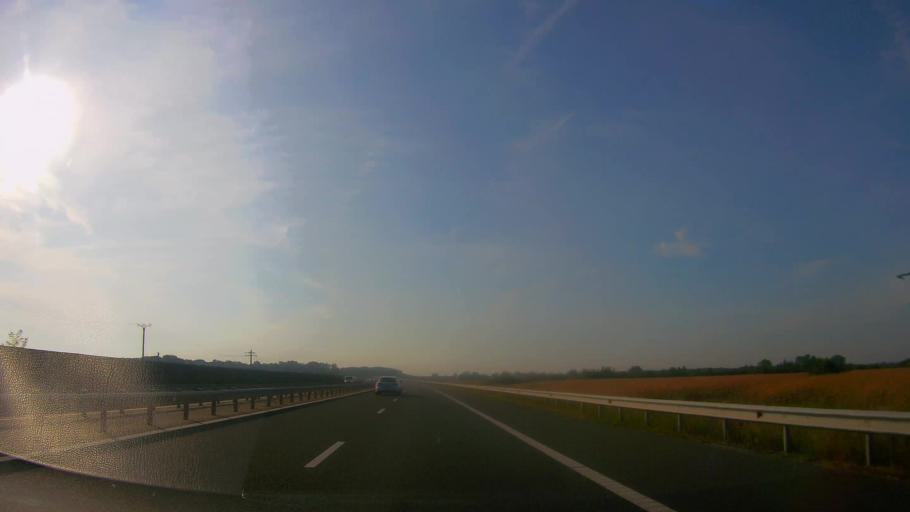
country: RO
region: Prahova
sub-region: Comuna Rafov
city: Rafov
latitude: 44.8676
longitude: 26.1429
